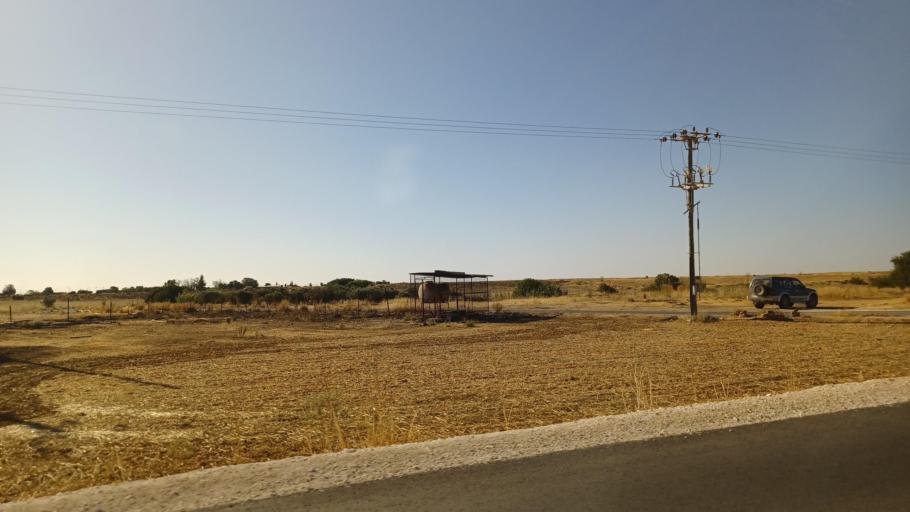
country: CY
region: Larnaka
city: Pergamos
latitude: 35.0264
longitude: 33.7047
